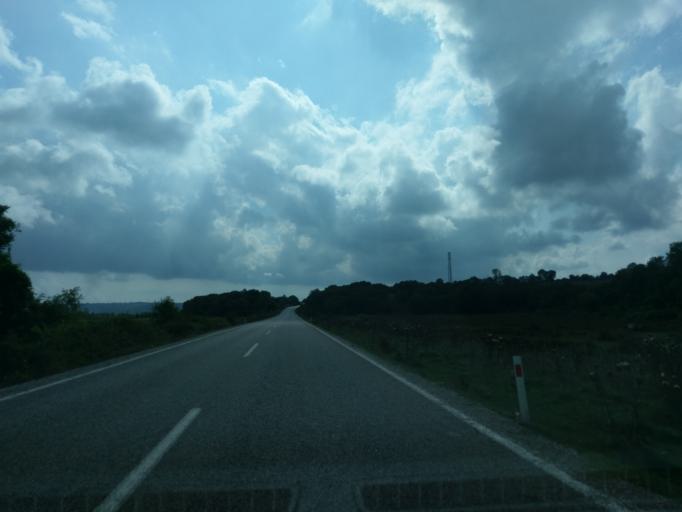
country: TR
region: Sinop
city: Sinop
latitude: 42.0248
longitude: 35.0422
